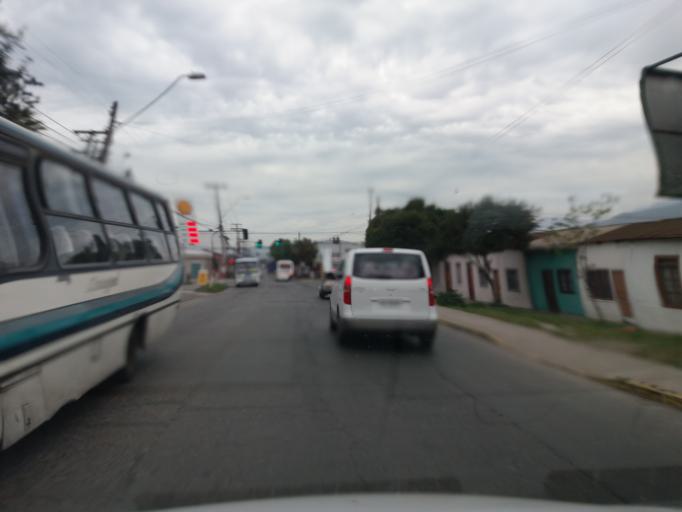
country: CL
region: Valparaiso
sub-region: Provincia de Quillota
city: Hacienda La Calera
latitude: -32.7784
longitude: -71.1914
